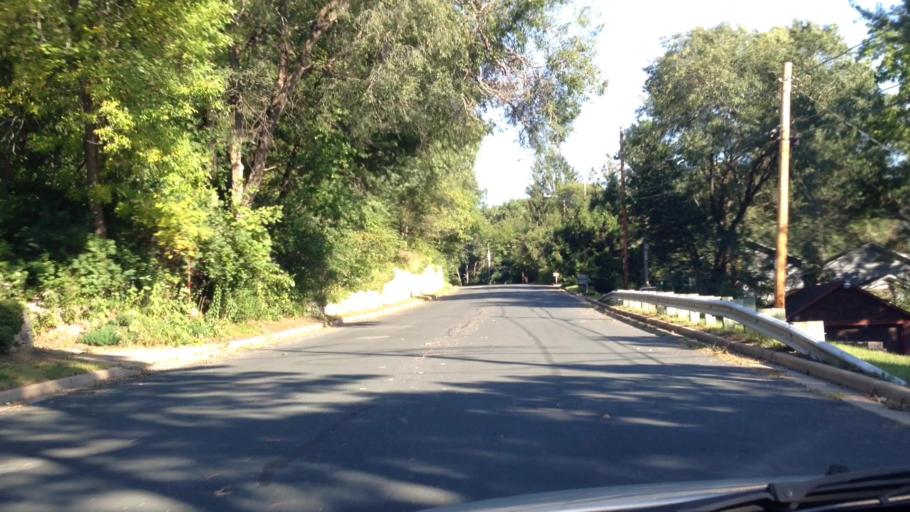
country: US
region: Wisconsin
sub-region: Saint Croix County
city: North Hudson
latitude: 44.9895
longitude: -92.7499
